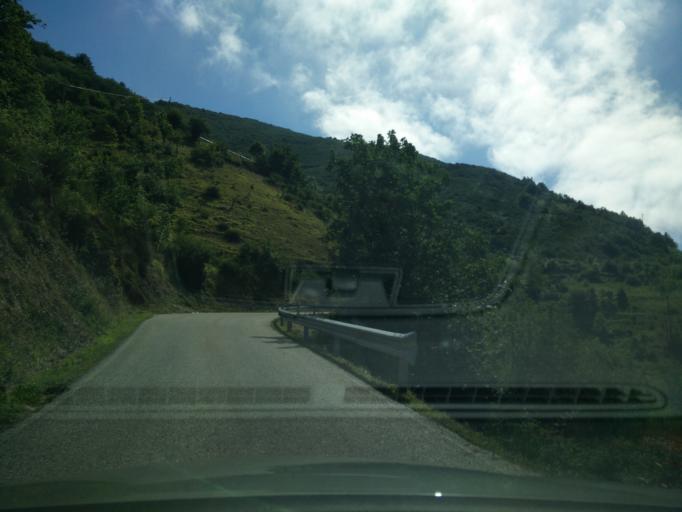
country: ES
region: Asturias
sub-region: Province of Asturias
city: Pola de Somiedo
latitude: 43.0788
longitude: -6.2257
